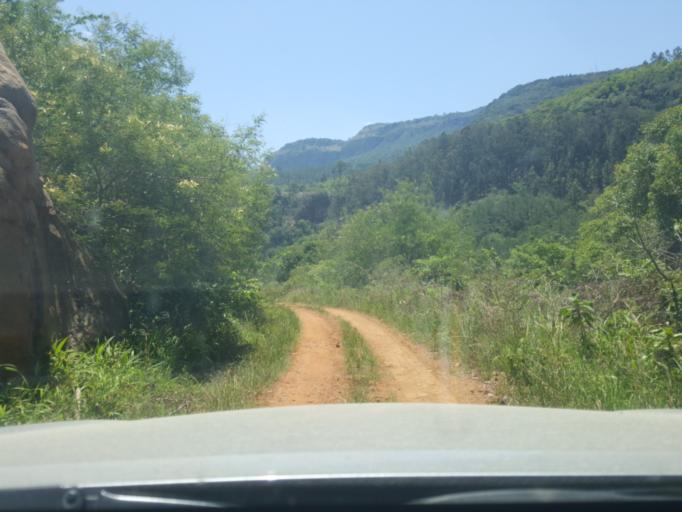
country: ZA
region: Limpopo
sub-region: Mopani District Municipality
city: Hoedspruit
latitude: -24.5972
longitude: 30.8520
